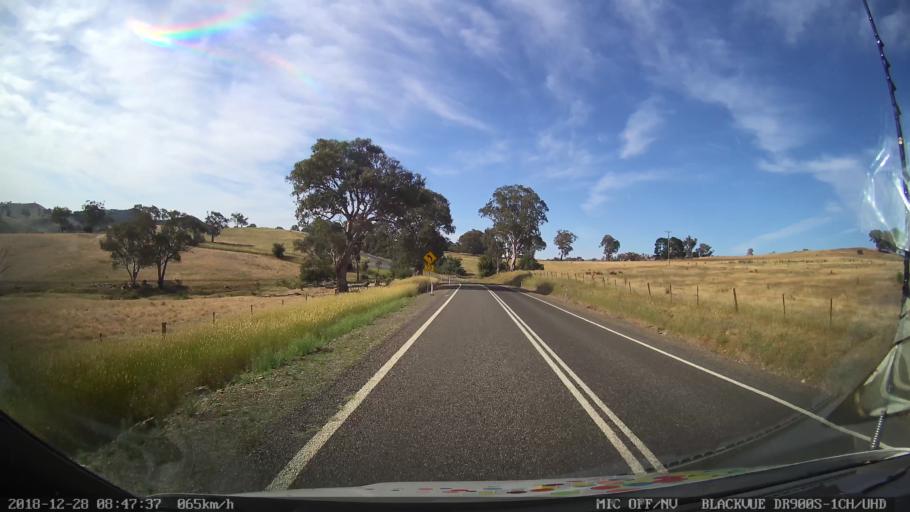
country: AU
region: New South Wales
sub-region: Upper Lachlan Shire
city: Crookwell
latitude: -34.0294
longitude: 149.3360
